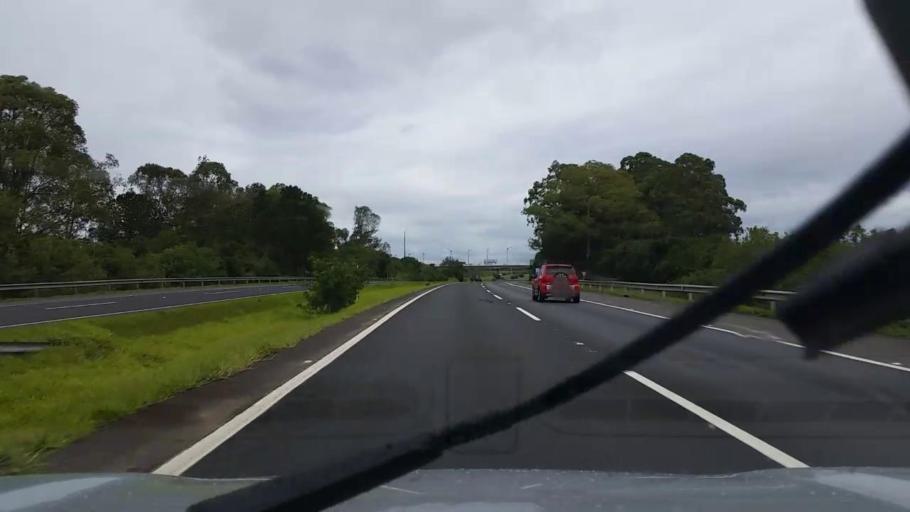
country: BR
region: Rio Grande do Sul
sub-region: Osorio
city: Osorio
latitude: -29.8917
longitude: -50.2814
